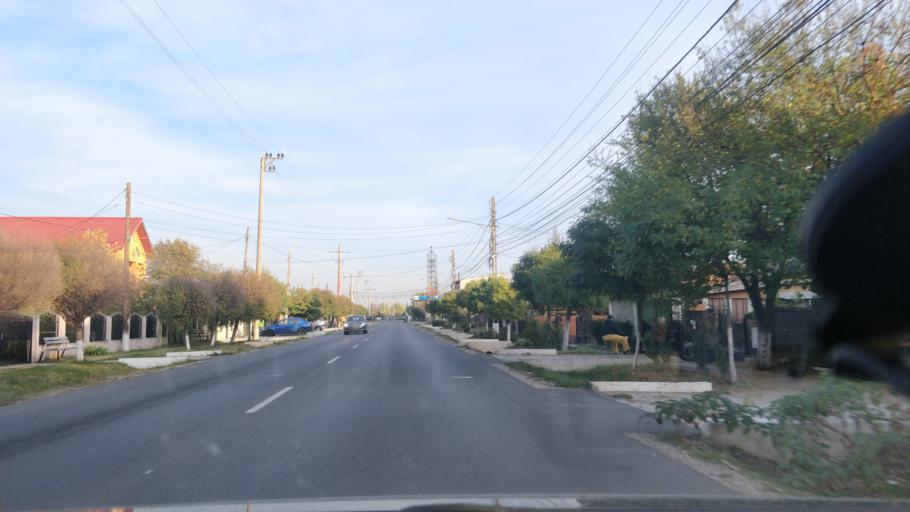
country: RO
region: Ilfov
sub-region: Comuna Ciorogarla
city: Ciorogarla
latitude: 44.4429
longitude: 25.8943
